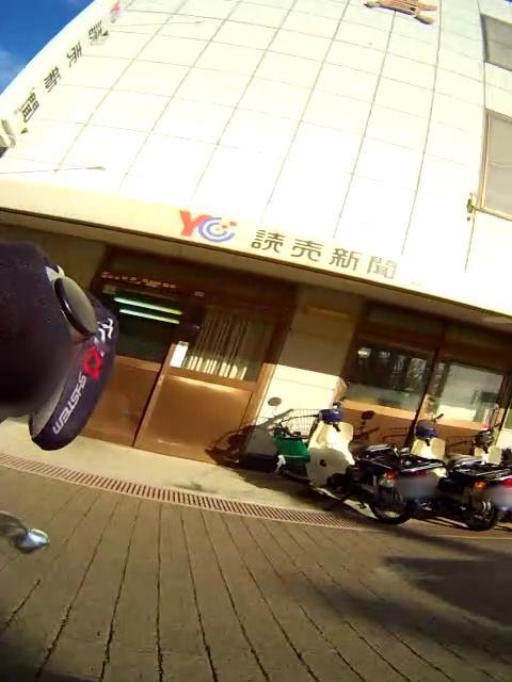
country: JP
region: Hyogo
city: Takarazuka
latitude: 34.7751
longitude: 135.3583
